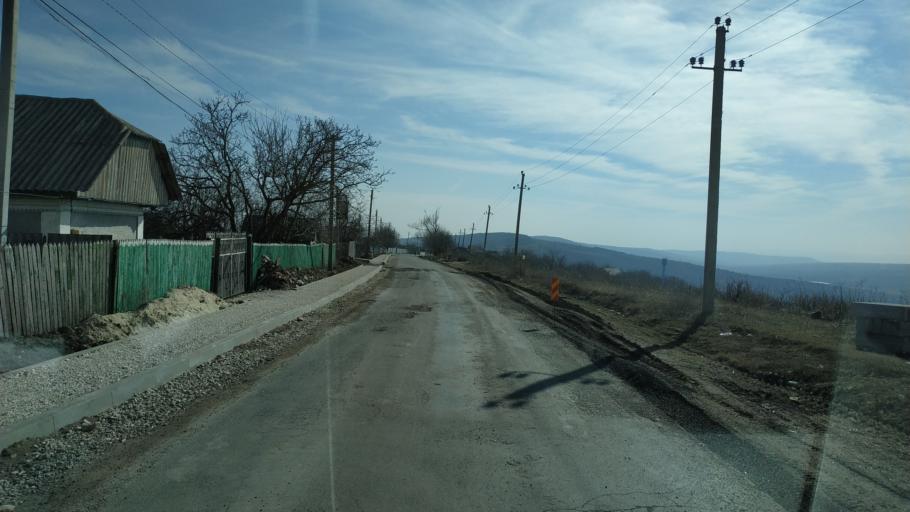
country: MD
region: Nisporeni
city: Nisporeni
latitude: 47.2037
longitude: 28.0599
